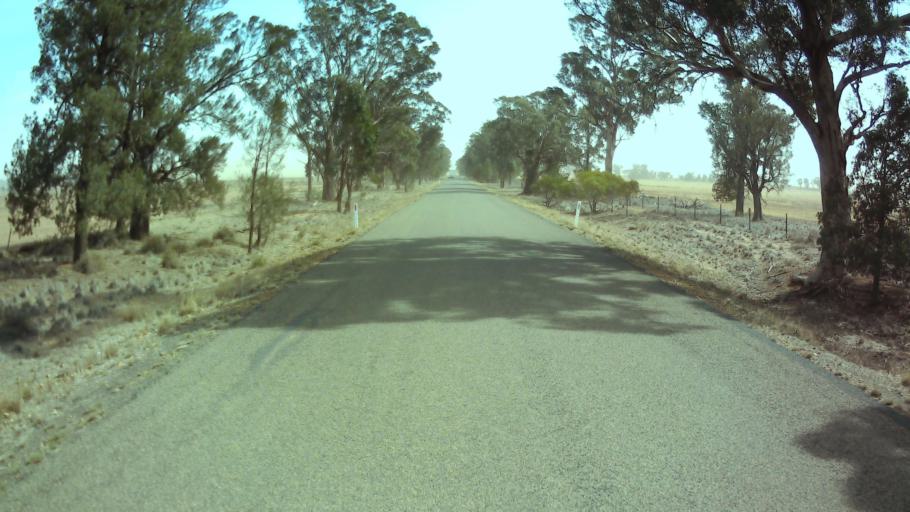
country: AU
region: New South Wales
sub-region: Weddin
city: Grenfell
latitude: -33.7593
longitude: 147.9891
